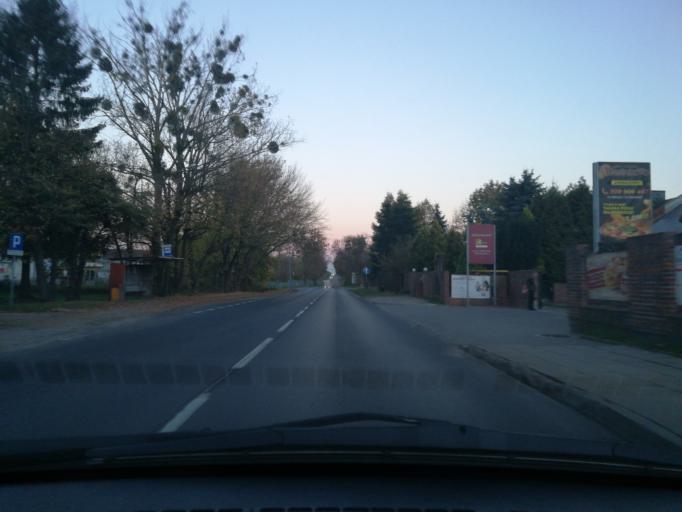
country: PL
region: Lodz Voivodeship
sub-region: Powiat lodzki wschodni
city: Andrespol
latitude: 51.7937
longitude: 19.5910
